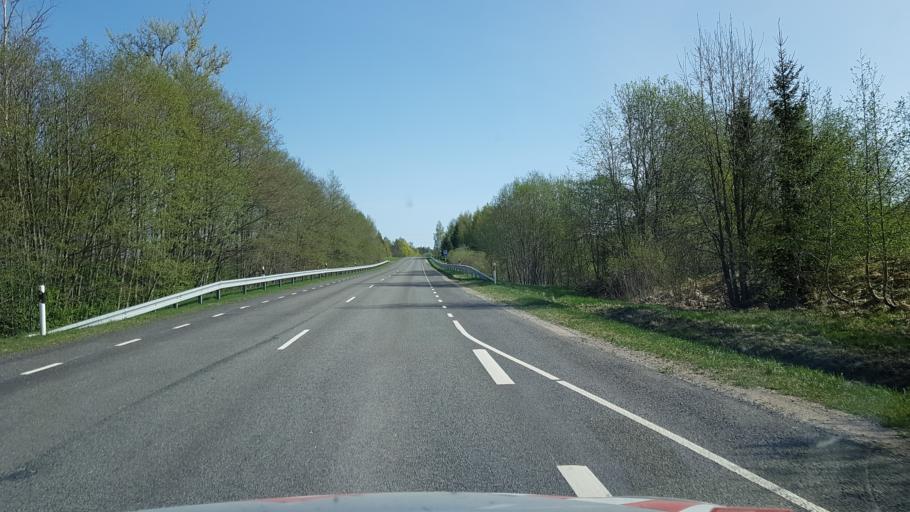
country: EE
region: Viljandimaa
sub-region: Viljandi linn
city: Viljandi
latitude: 58.2354
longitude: 25.5847
